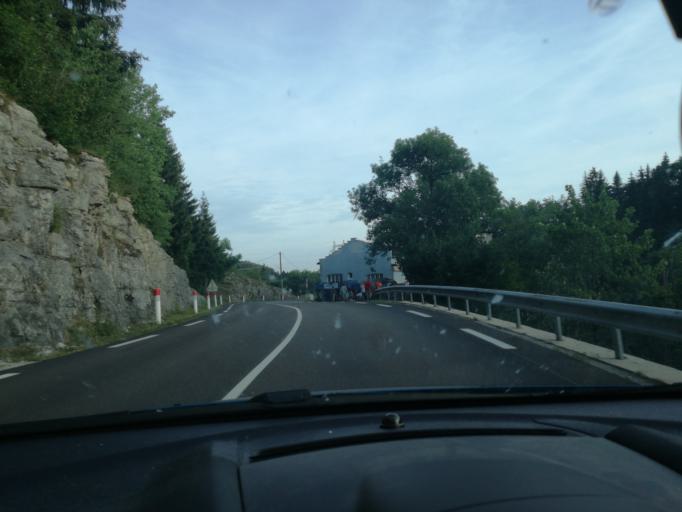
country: FR
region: Franche-Comte
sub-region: Departement du Jura
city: Morbier
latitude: 46.6227
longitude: 5.9606
